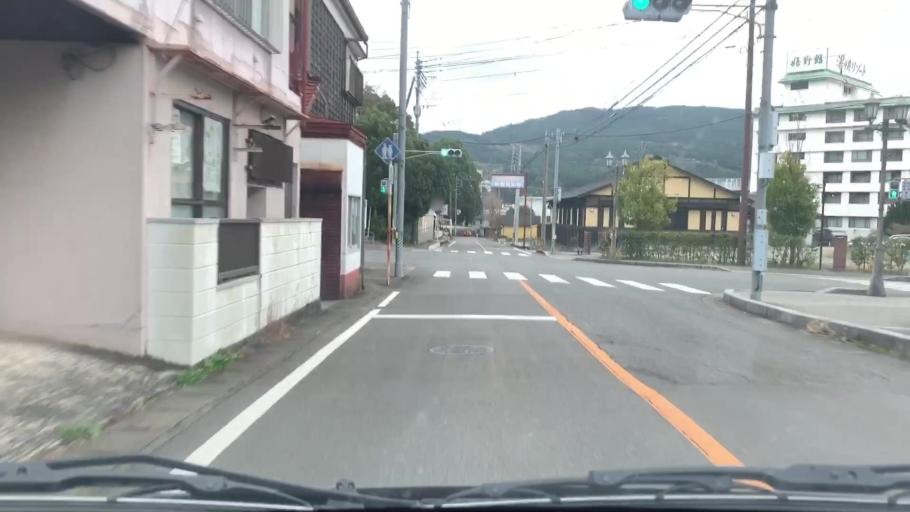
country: JP
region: Saga Prefecture
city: Ureshinomachi-shimojuku
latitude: 33.0996
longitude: 129.9807
